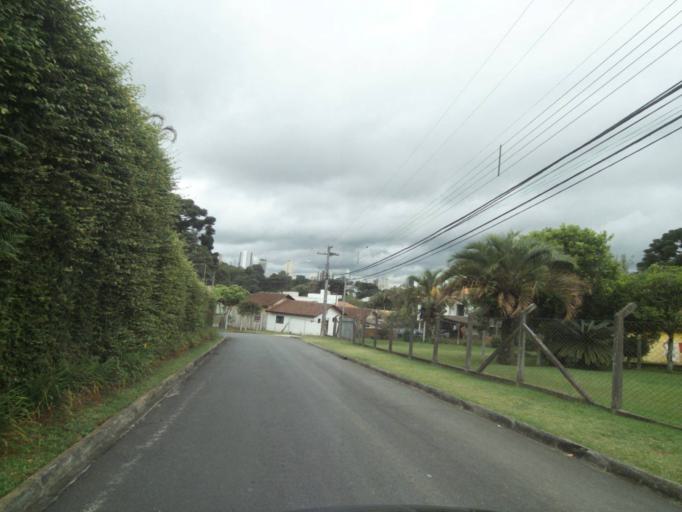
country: BR
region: Parana
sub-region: Curitiba
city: Curitiba
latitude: -25.4503
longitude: -49.3349
